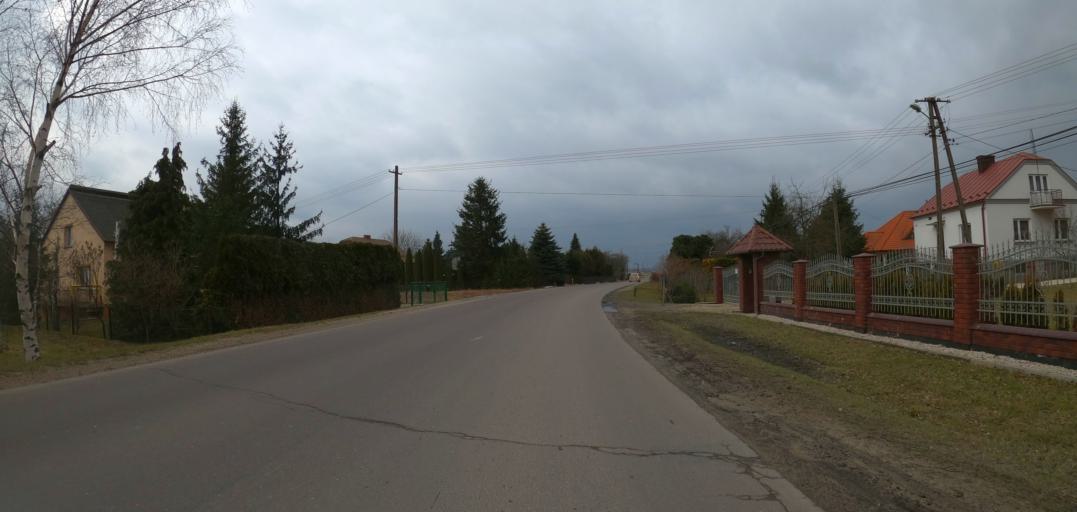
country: PL
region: Subcarpathian Voivodeship
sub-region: Powiat debicki
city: Pilzno
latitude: 49.9878
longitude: 21.3147
